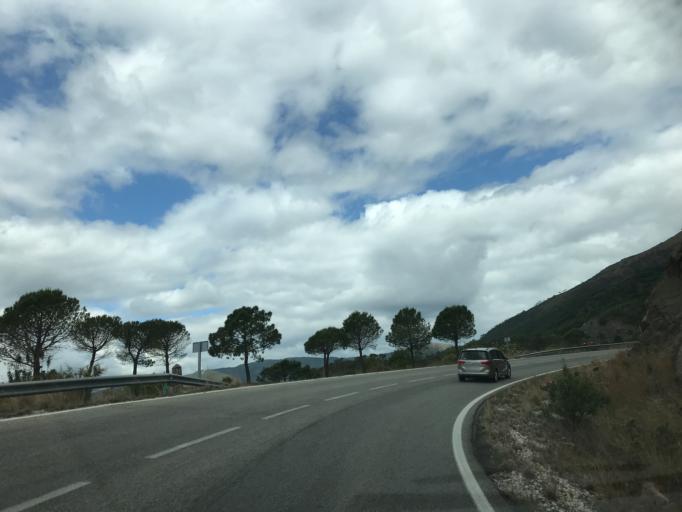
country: ES
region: Andalusia
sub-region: Provincia de Malaga
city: Benahavis
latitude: 36.5509
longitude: -5.0297
